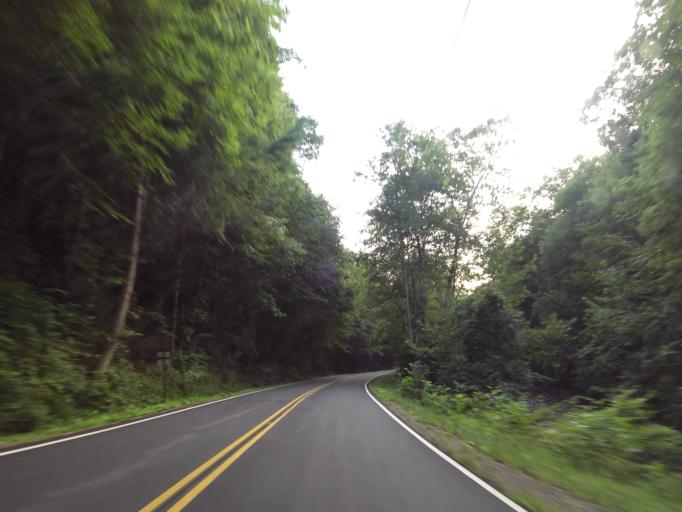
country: US
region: Tennessee
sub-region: Johnson County
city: Mountain City
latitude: 36.5927
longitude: -81.8161
